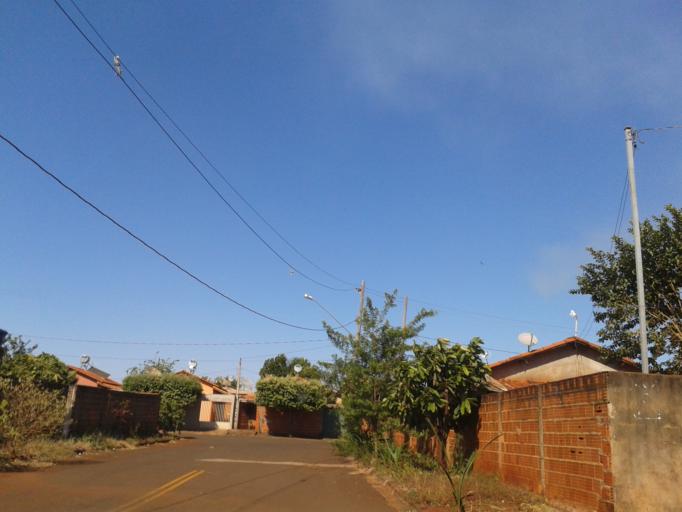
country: BR
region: Minas Gerais
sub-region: Capinopolis
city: Capinopolis
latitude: -18.5203
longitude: -49.5031
